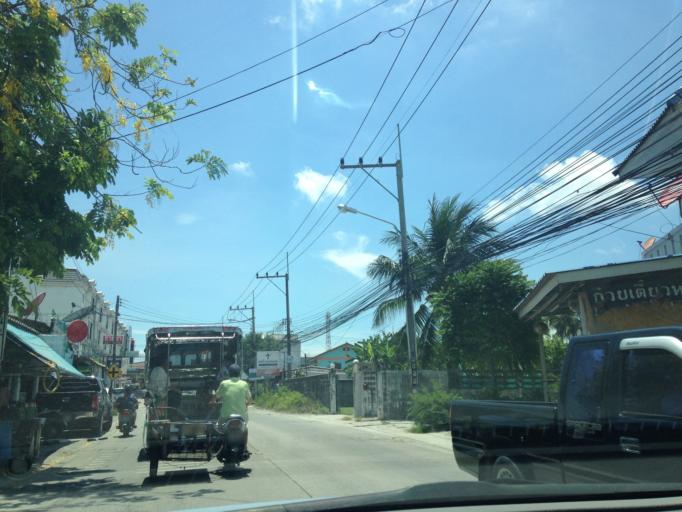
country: TH
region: Chon Buri
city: Chon Buri
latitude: 13.2964
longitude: 100.9362
